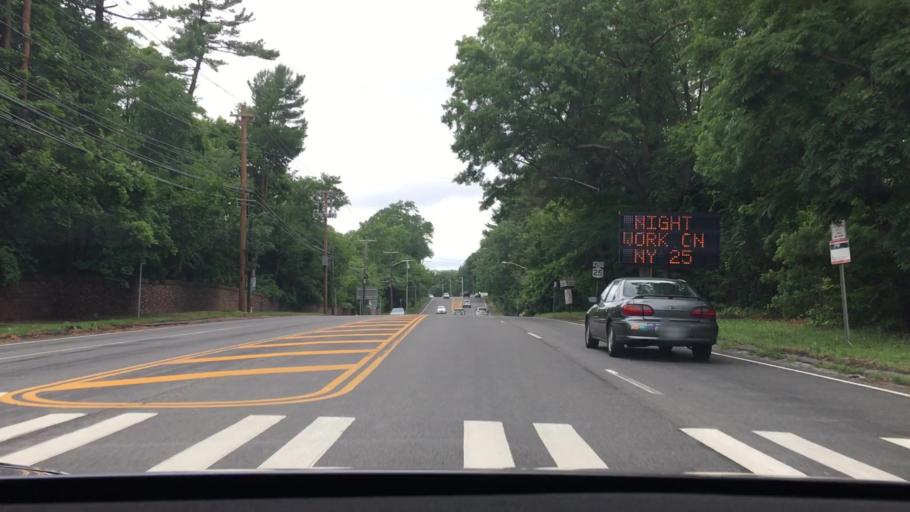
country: US
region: New York
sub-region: Nassau County
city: Woodbury
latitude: 40.8196
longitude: -73.4528
